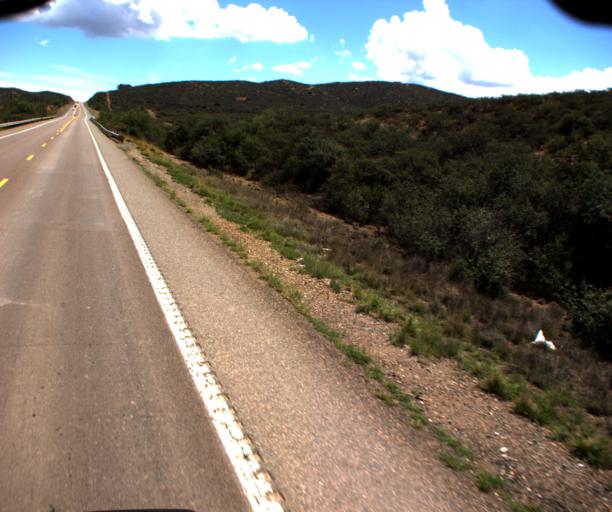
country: US
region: Arizona
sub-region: Yavapai County
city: Dewey-Humboldt
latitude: 34.5400
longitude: -112.1991
